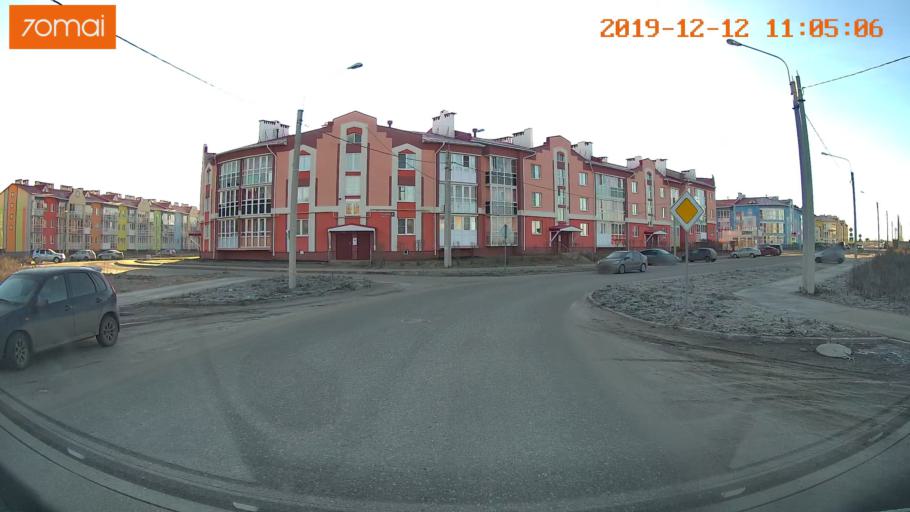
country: RU
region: Ivanovo
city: Kokhma
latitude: 56.9506
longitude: 41.1017
